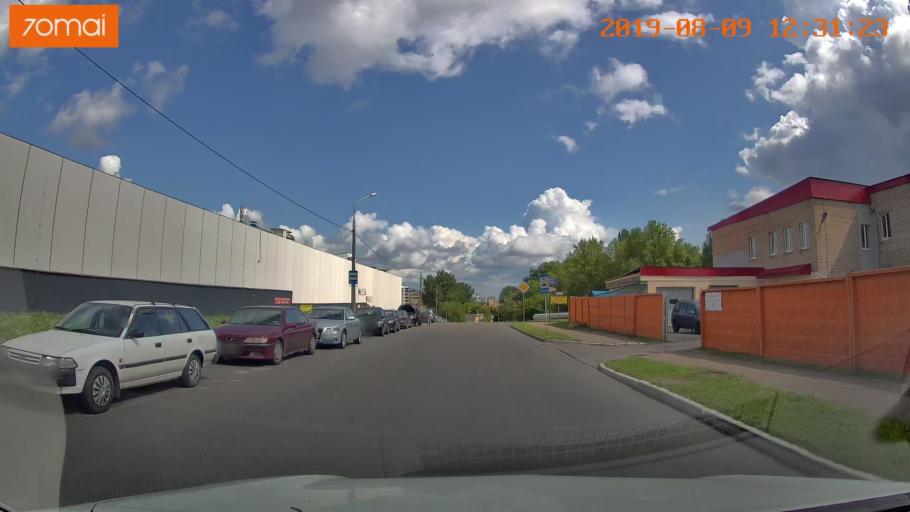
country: BY
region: Minsk
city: Minsk
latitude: 53.9190
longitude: 27.5076
